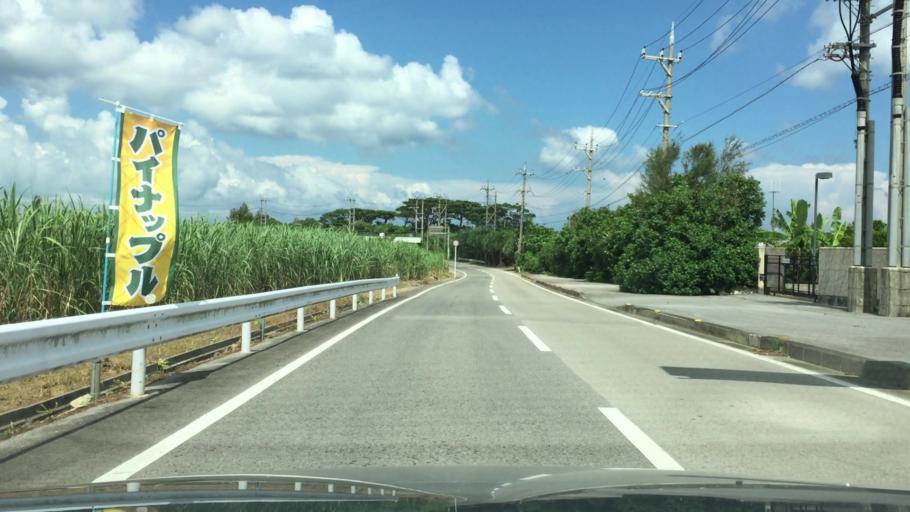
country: JP
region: Okinawa
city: Ishigaki
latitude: 24.3951
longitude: 124.1557
